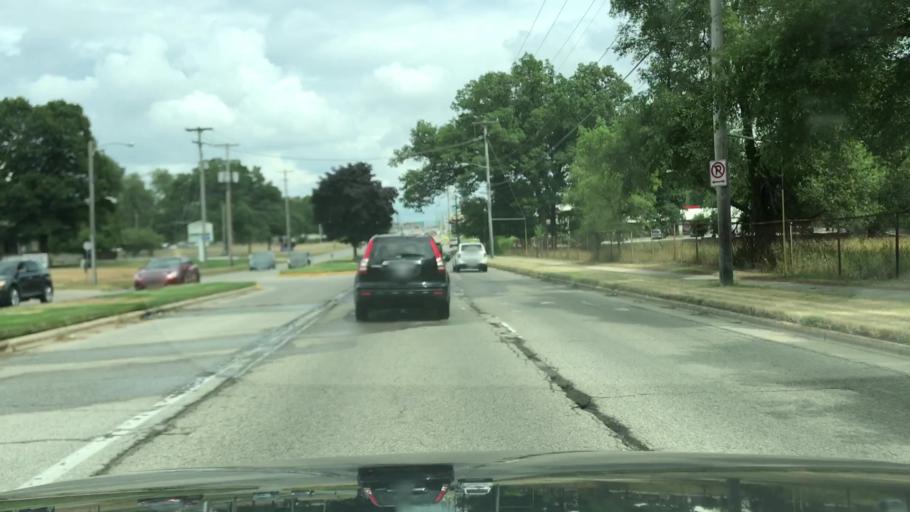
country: US
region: Michigan
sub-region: Kent County
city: Wyoming
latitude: 42.8842
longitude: -85.6910
